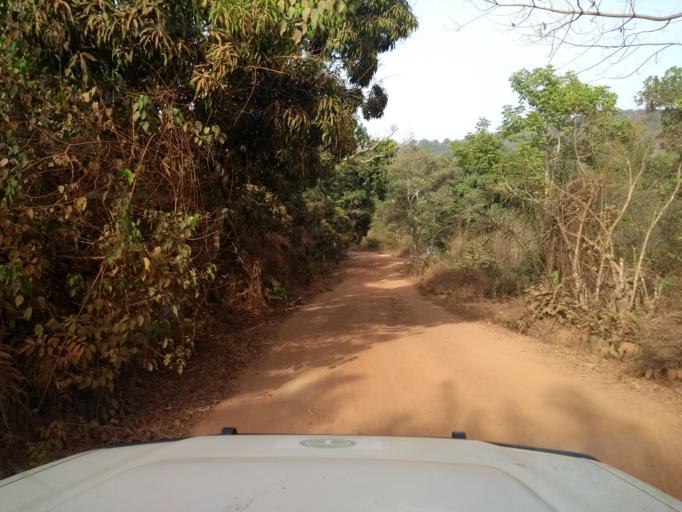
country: GN
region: Kindia
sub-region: Prefecture de Dubreka
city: Dubreka
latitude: 9.8549
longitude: -13.5506
